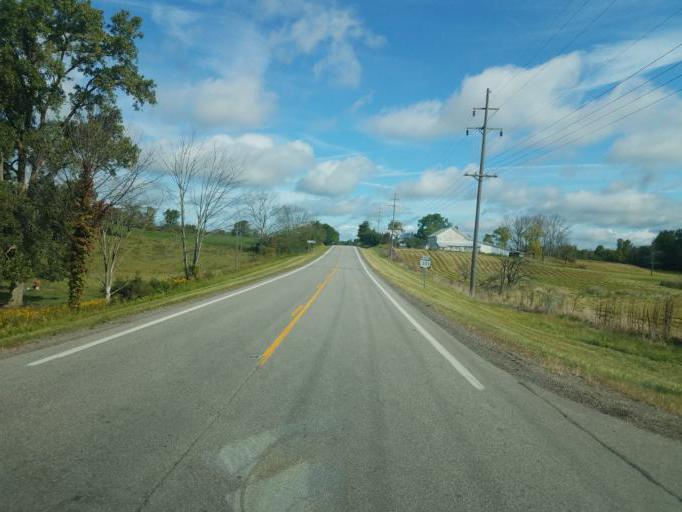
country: US
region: Ohio
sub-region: Wayne County
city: West Salem
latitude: 41.0563
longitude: -82.1256
